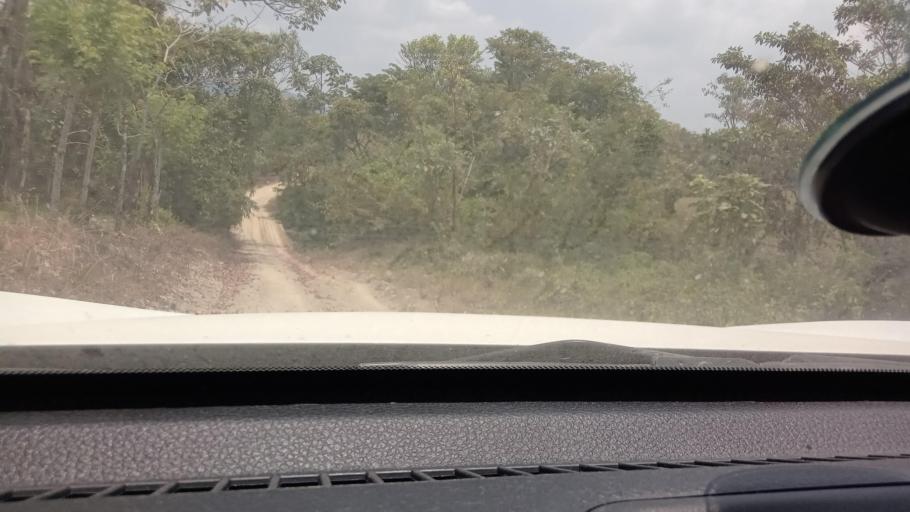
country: MX
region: Tabasco
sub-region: Huimanguillo
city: Francisco Rueda
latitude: 17.4893
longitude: -93.9319
